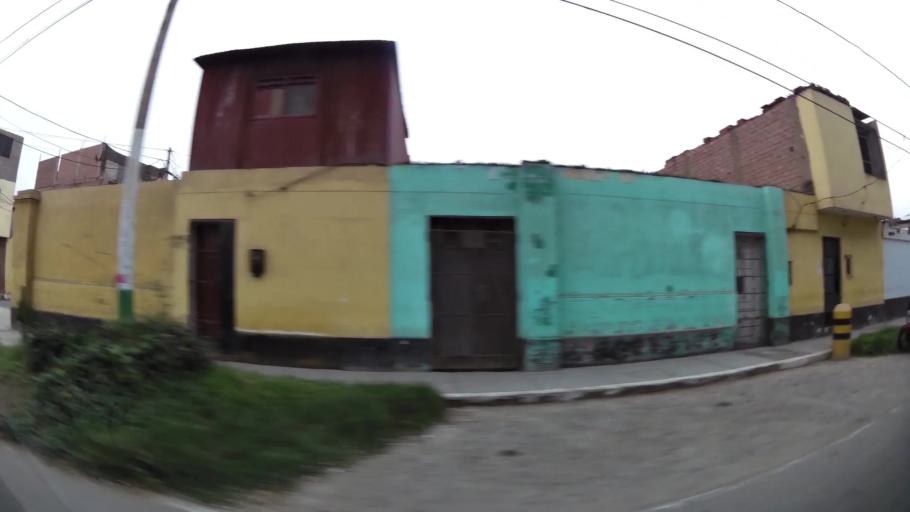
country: PE
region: Callao
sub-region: Callao
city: Callao
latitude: -12.0723
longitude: -77.1241
